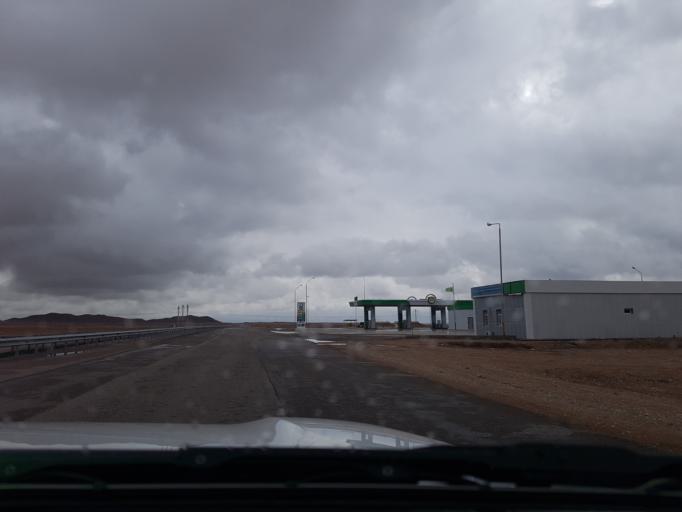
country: TM
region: Balkan
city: Balkanabat
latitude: 39.9306
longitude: 53.8641
